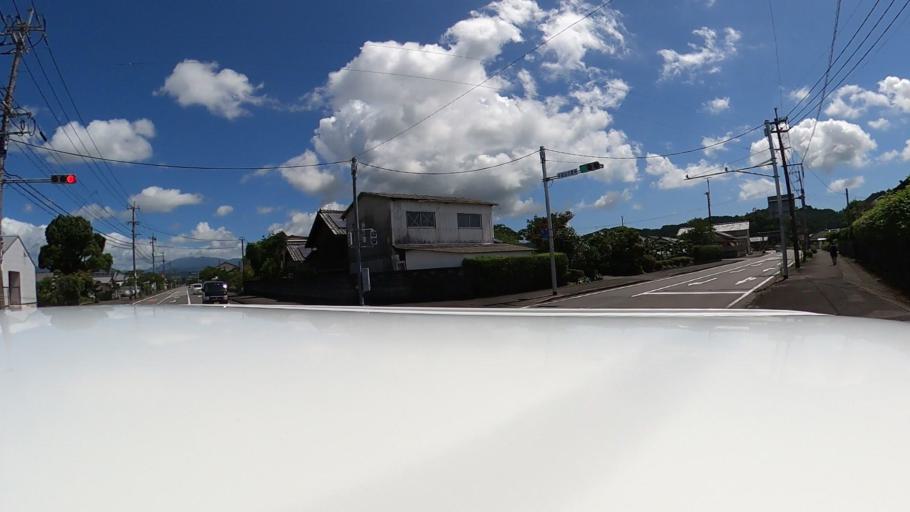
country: JP
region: Miyazaki
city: Tsuma
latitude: 32.1007
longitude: 131.4090
